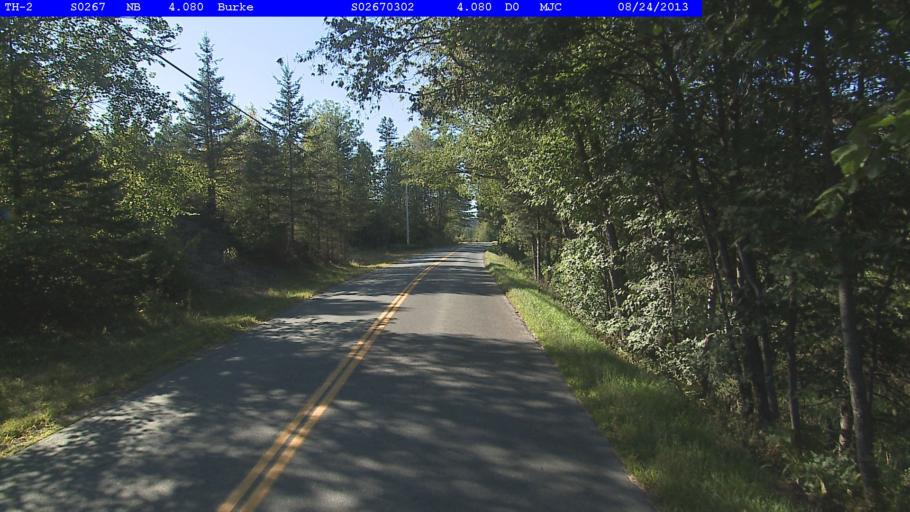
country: US
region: Vermont
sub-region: Caledonia County
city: Lyndonville
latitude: 44.6333
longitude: -71.9680
